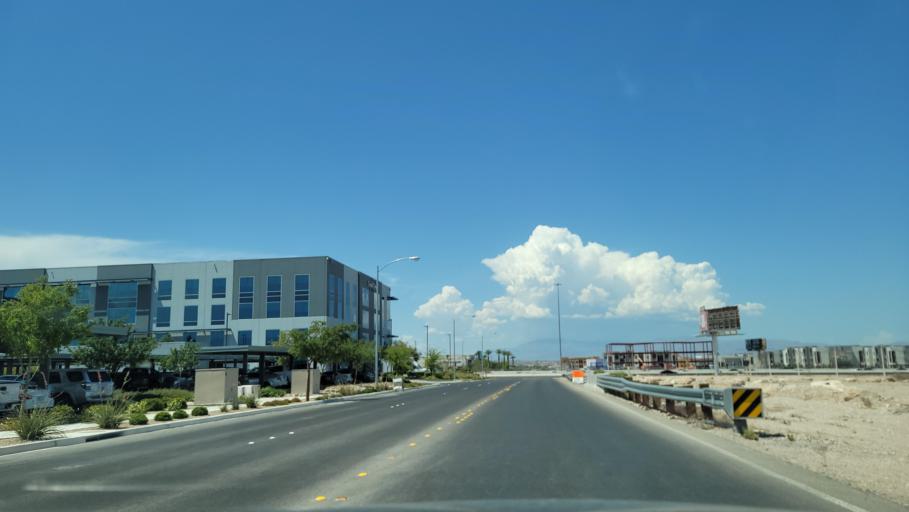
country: US
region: Nevada
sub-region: Clark County
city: Enterprise
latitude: 36.0640
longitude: -115.2702
